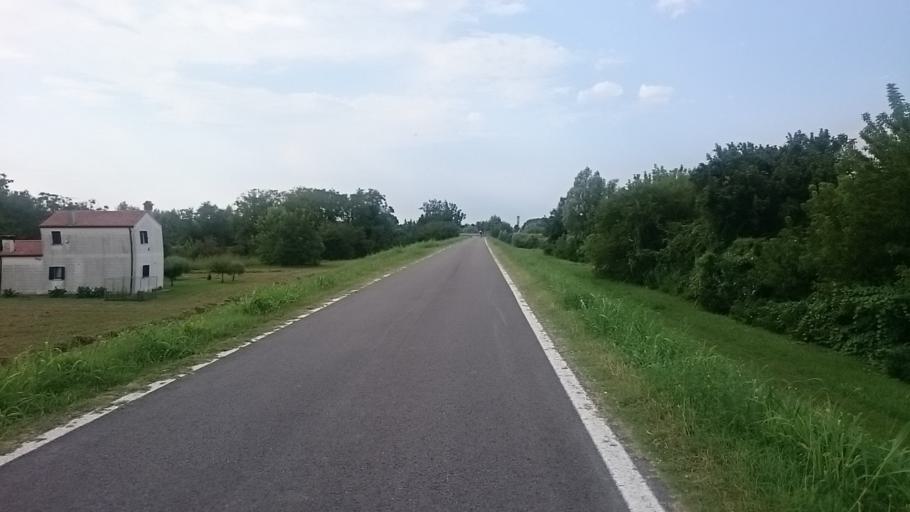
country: IT
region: Veneto
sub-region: Provincia di Padova
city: Casalserugo
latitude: 45.3009
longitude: 11.9288
